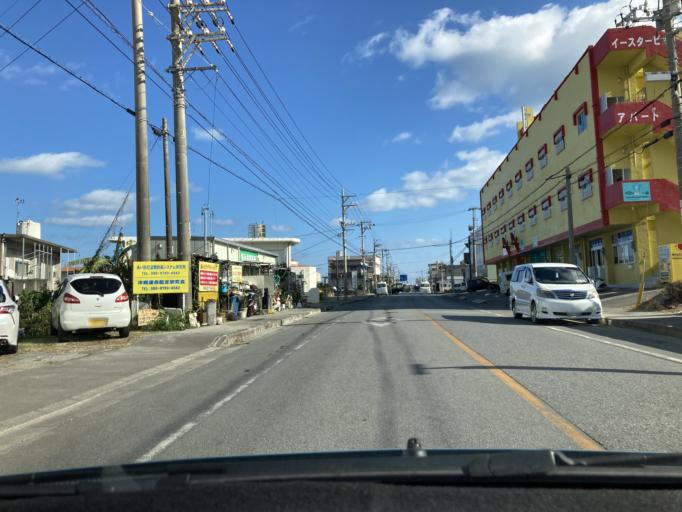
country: JP
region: Okinawa
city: Katsuren-haebaru
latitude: 26.3101
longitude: 127.9095
